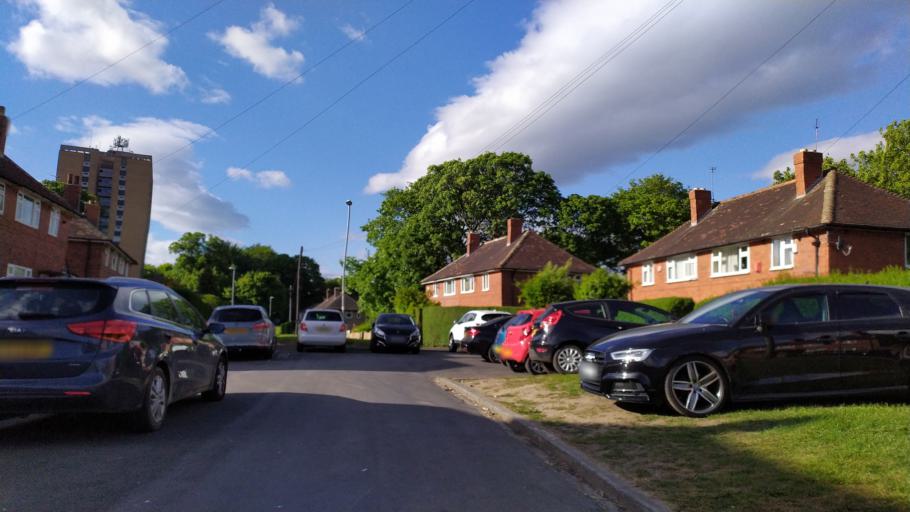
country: GB
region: England
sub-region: City and Borough of Leeds
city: Chapel Allerton
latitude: 53.8236
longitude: -1.5402
